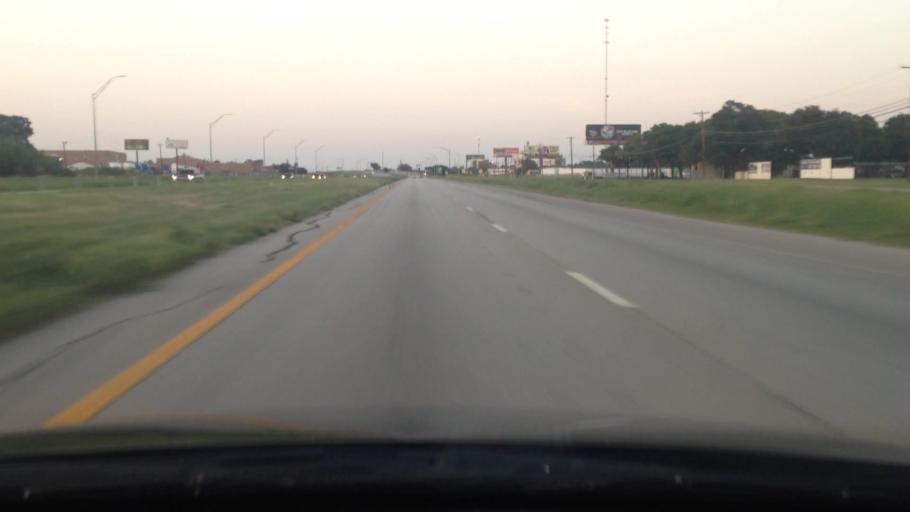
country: US
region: Texas
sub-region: Tarrant County
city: Forest Hill
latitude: 32.7123
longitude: -97.2290
